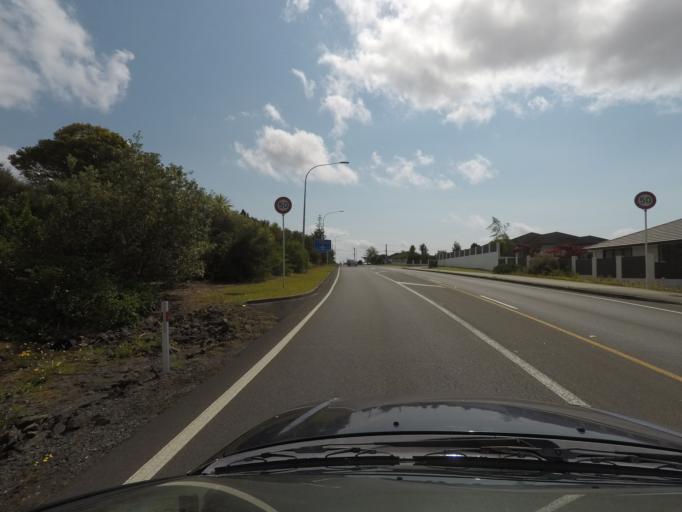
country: NZ
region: Northland
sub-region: Whangarei
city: Whangarei
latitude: -35.6888
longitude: 174.3221
